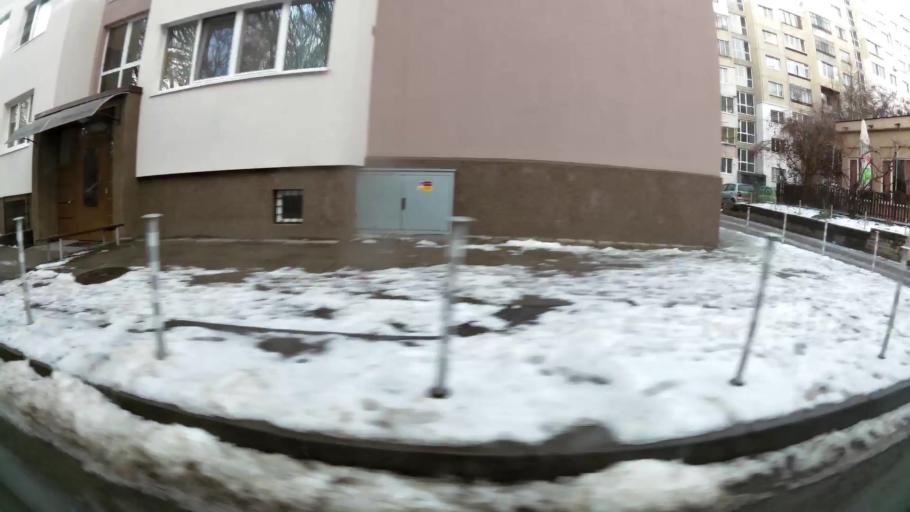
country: BG
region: Sofia-Capital
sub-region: Stolichna Obshtina
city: Sofia
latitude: 42.6969
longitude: 23.2914
